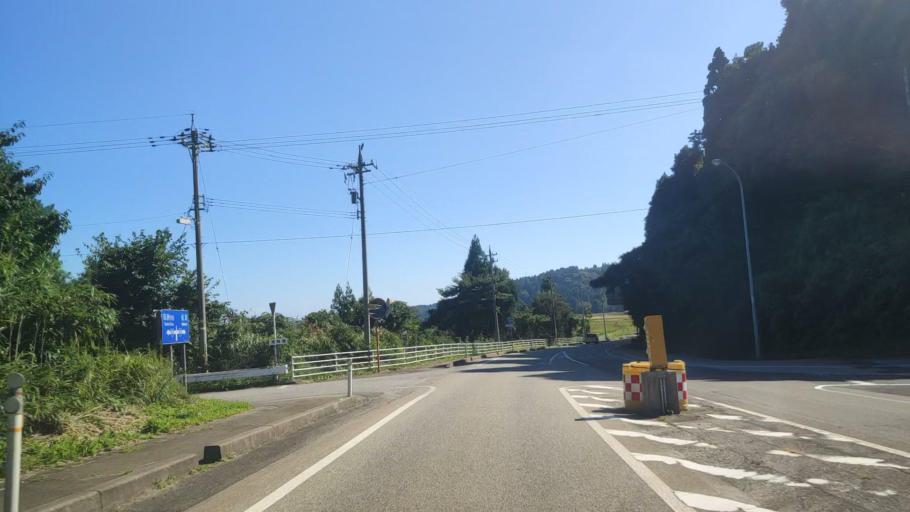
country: JP
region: Ishikawa
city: Nanao
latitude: 37.3930
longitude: 137.2342
